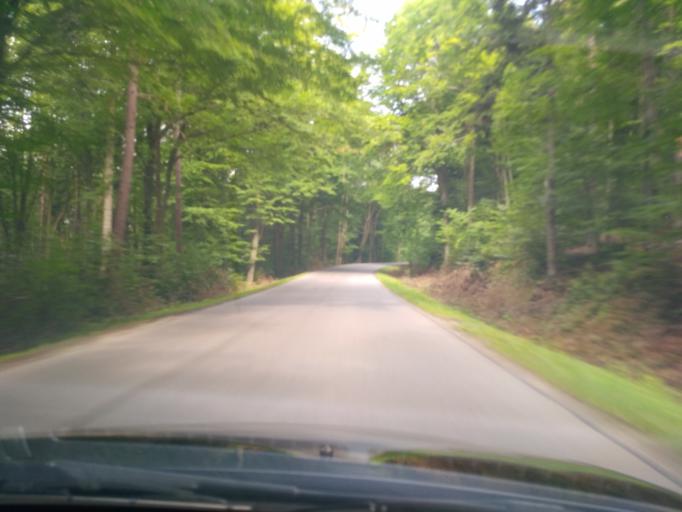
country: PL
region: Subcarpathian Voivodeship
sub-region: Powiat strzyzowski
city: Czudec
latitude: 49.9683
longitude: 21.8391
